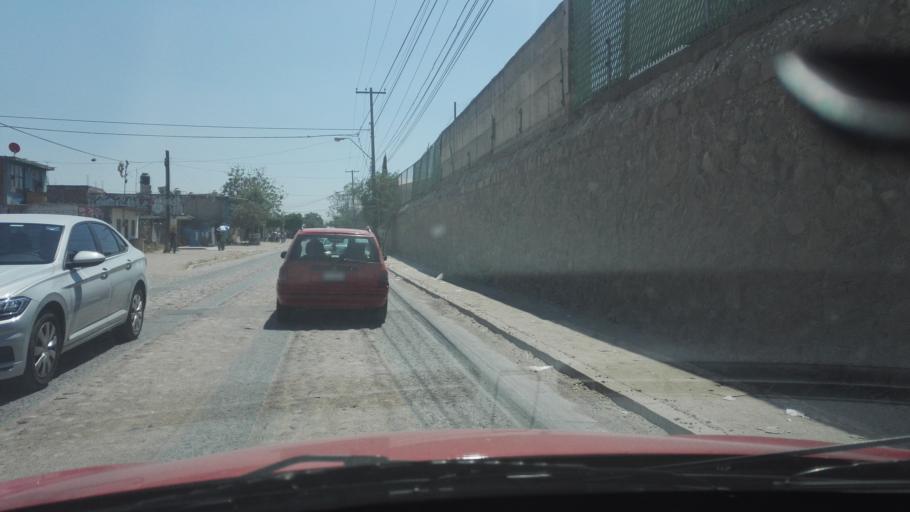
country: MX
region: Guanajuato
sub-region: Leon
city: Fraccionamiento Paraiso Real
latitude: 21.0955
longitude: -101.6016
